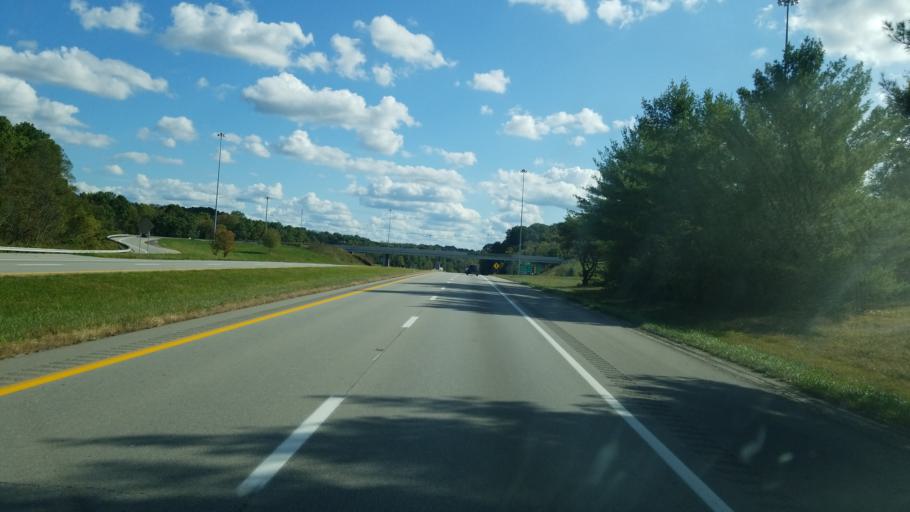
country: US
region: Ohio
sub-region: Guernsey County
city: Cambridge
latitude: 40.0518
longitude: -81.5644
